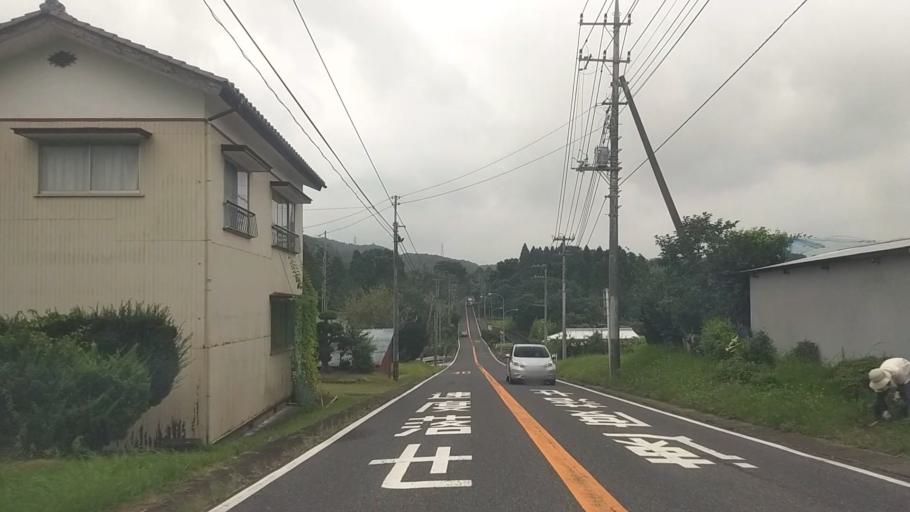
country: JP
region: Chiba
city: Kisarazu
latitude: 35.2813
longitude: 140.0789
